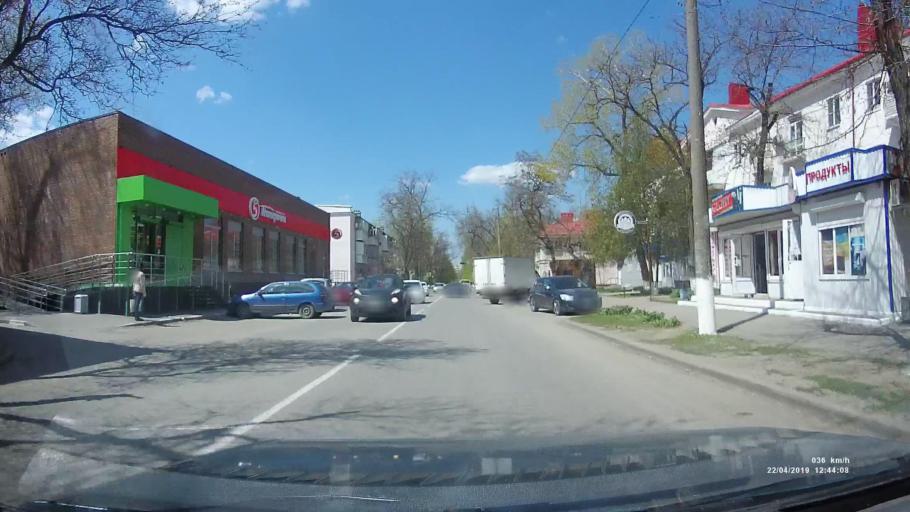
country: RU
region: Rostov
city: Azov
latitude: 47.1032
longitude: 39.4192
